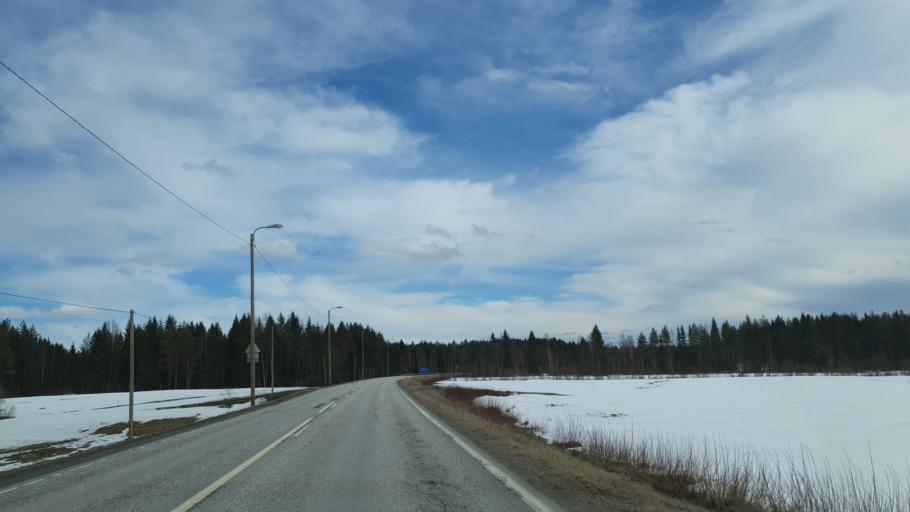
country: FI
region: Kainuu
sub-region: Kajaani
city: Vuokatti
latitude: 64.1691
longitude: 28.2325
